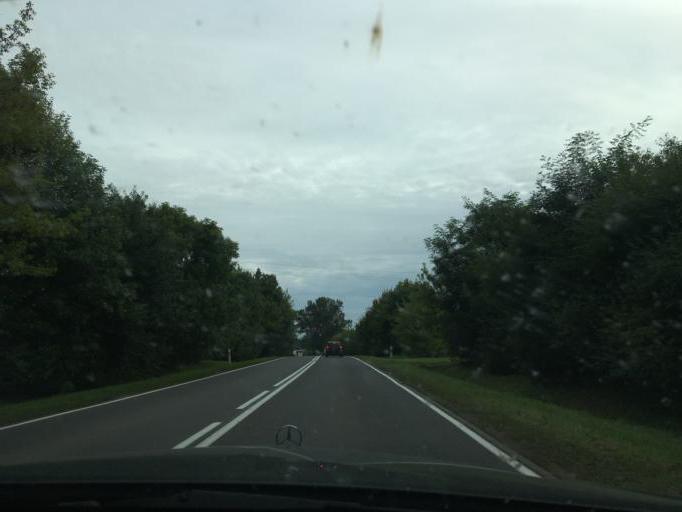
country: PL
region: Masovian Voivodeship
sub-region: Powiat ostrowski
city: Ostrow Mazowiecka
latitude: 52.8451
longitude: 21.8688
